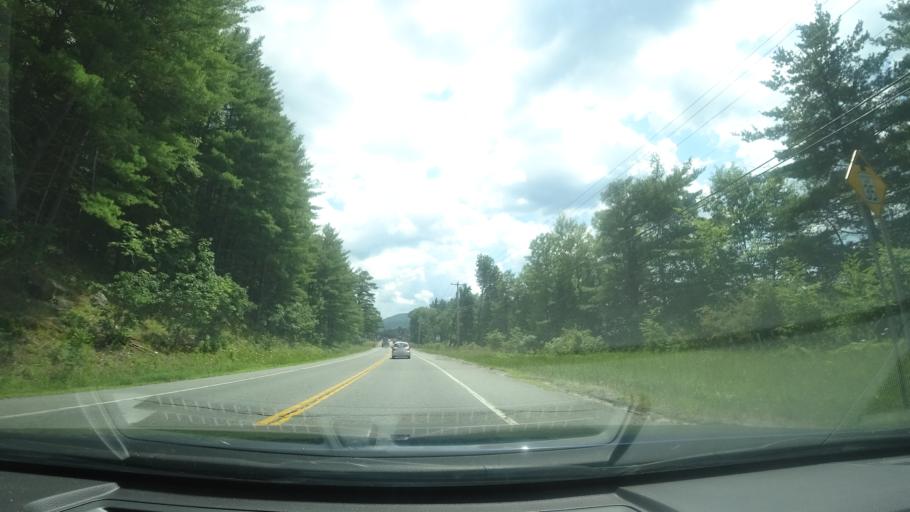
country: US
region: New York
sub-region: Warren County
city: Warrensburg
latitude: 43.5069
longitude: -73.7895
